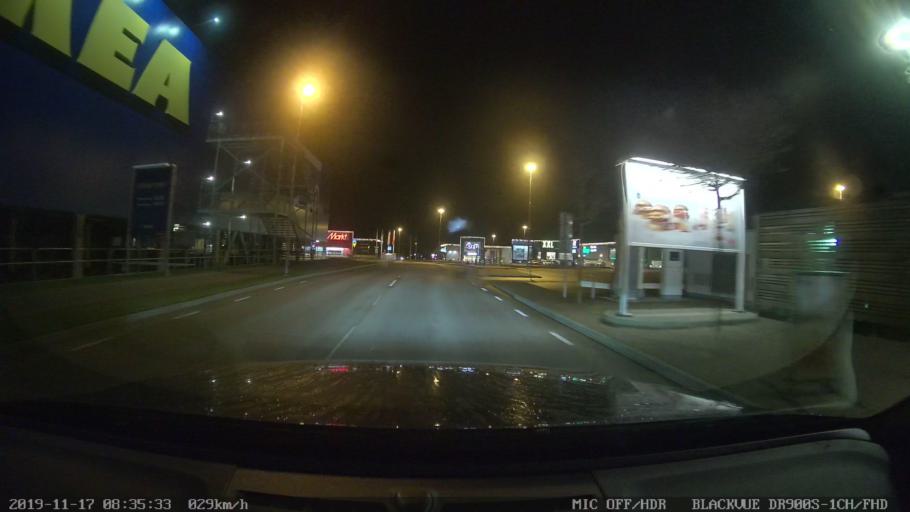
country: SE
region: Skane
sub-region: Helsingborg
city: Odakra
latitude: 56.0929
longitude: 12.7601
